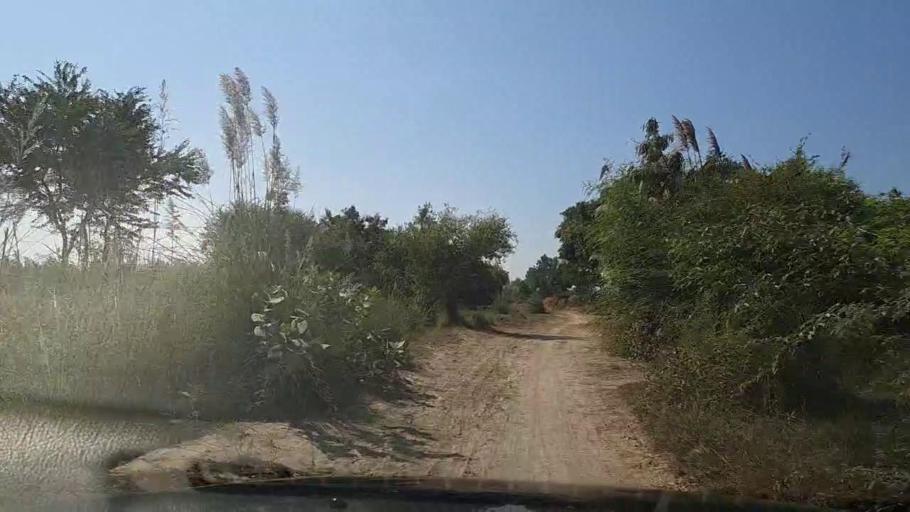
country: PK
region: Sindh
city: Mirpur Sakro
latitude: 24.5878
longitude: 67.8154
